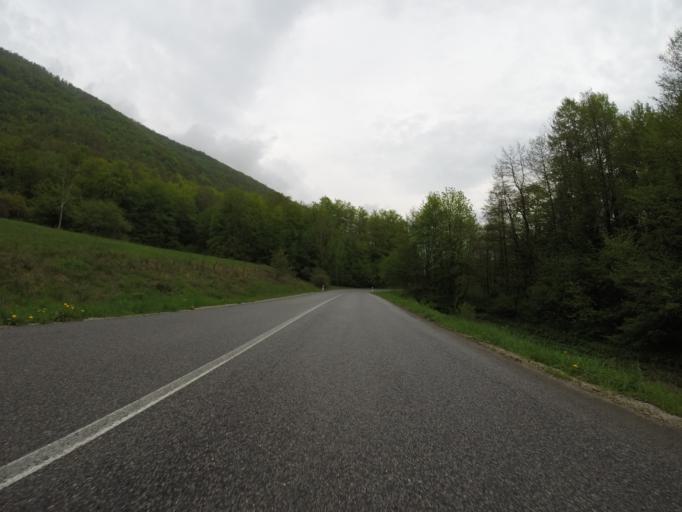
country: SK
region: Banskobystricky
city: Tisovec
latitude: 48.7231
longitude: 20.0112
